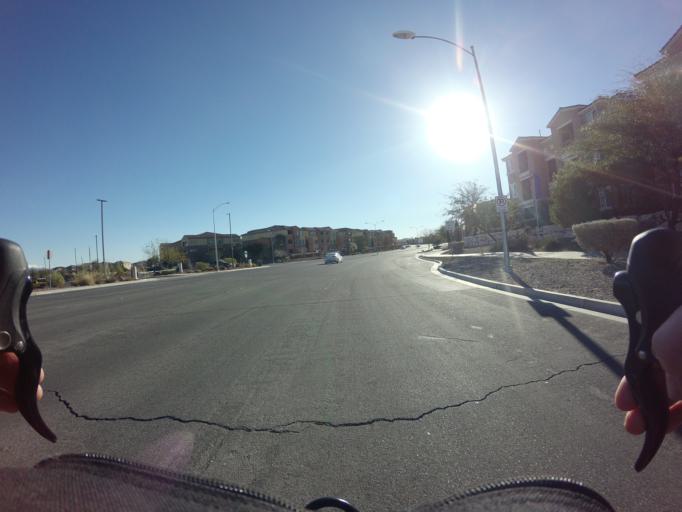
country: US
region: Nevada
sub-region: Clark County
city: Whitney
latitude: 36.0429
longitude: -115.0533
